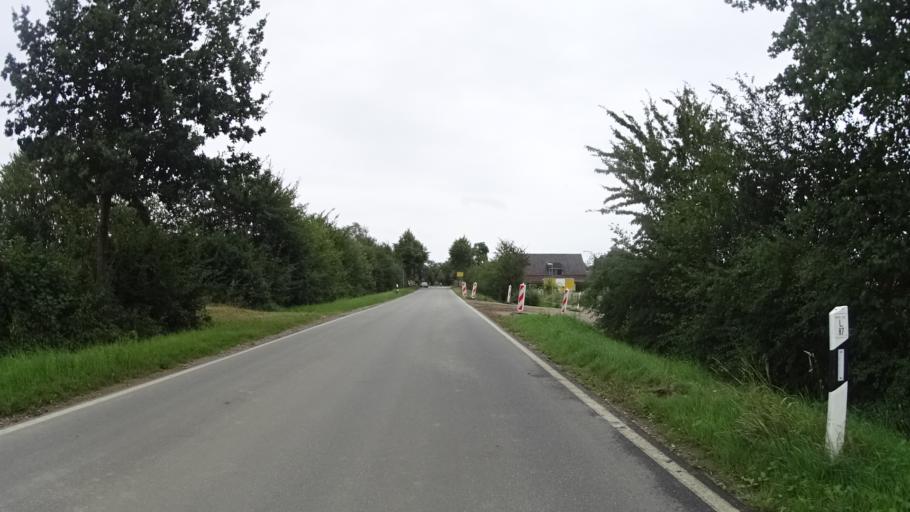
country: DE
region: Schleswig-Holstein
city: Labenz
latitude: 53.7134
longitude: 10.5123
